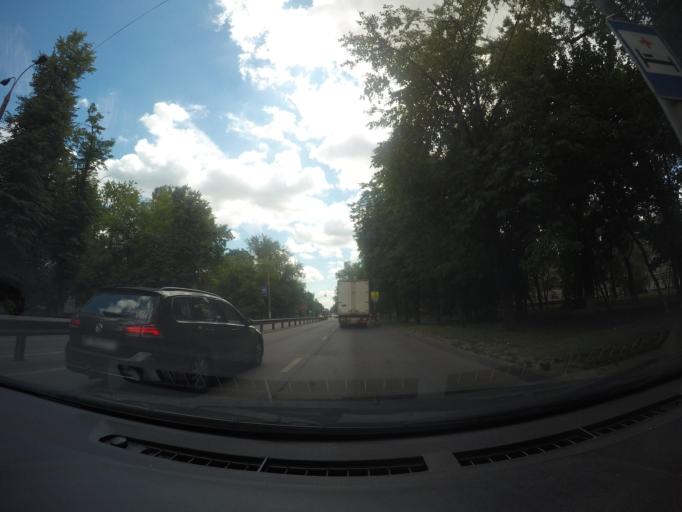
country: RU
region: Moskovskaya
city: Lyubertsy
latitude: 55.6671
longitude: 37.9082
